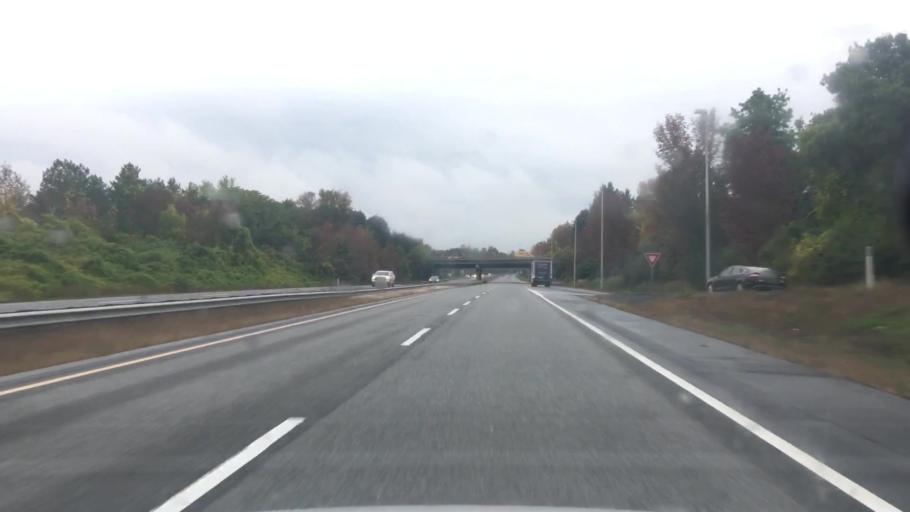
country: US
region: Maine
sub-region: Kennebec County
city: Augusta
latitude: 44.3142
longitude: -69.8104
